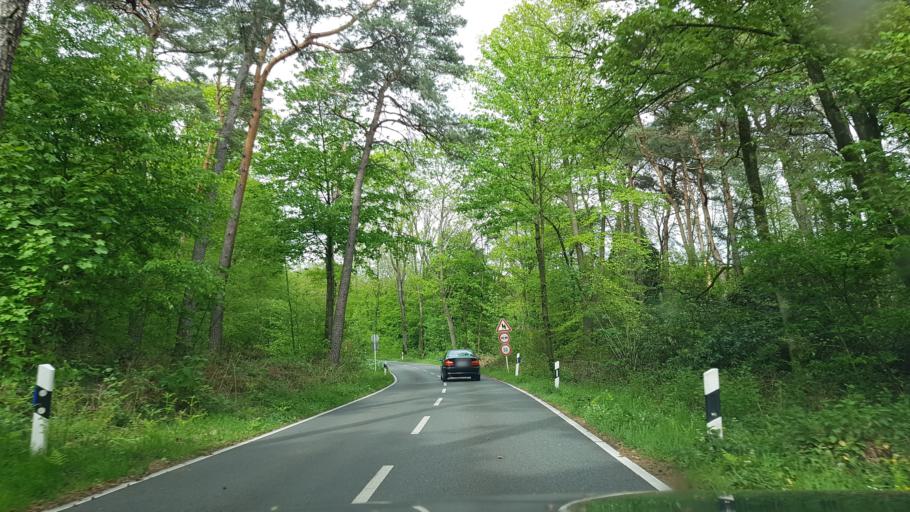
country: DE
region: North Rhine-Westphalia
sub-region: Regierungsbezirk Dusseldorf
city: Muelheim (Ruhr)
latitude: 51.3898
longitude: 6.8331
